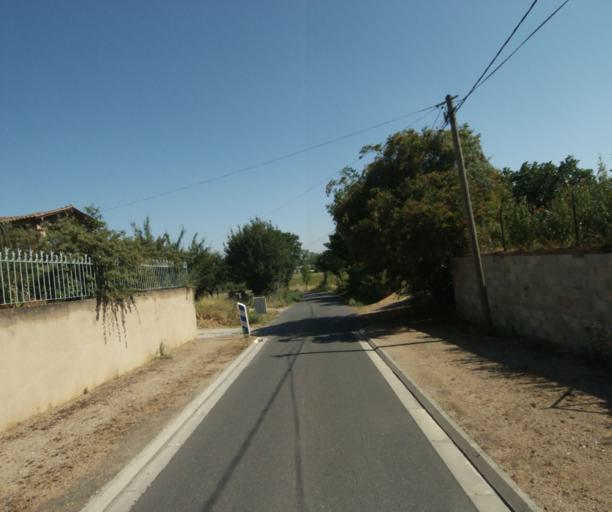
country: FR
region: Midi-Pyrenees
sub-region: Departement de la Haute-Garonne
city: Revel
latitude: 43.5043
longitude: 1.9486
